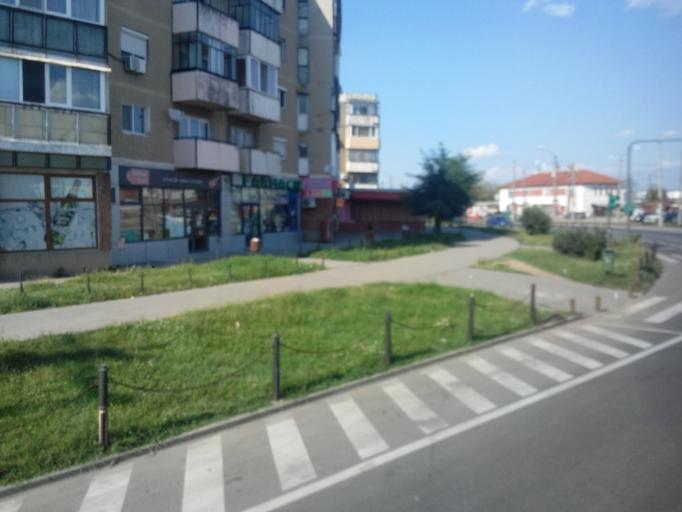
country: RO
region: Arad
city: Arad
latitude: 46.1442
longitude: 21.3332
